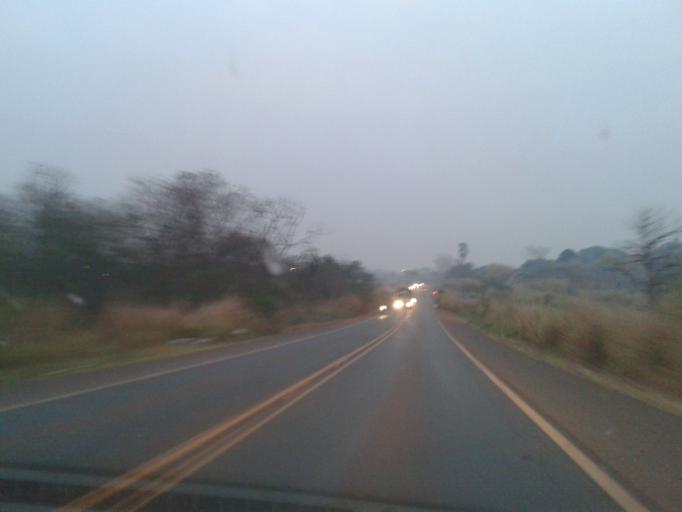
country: BR
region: Minas Gerais
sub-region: Ituiutaba
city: Ituiutaba
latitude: -18.9574
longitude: -49.4698
